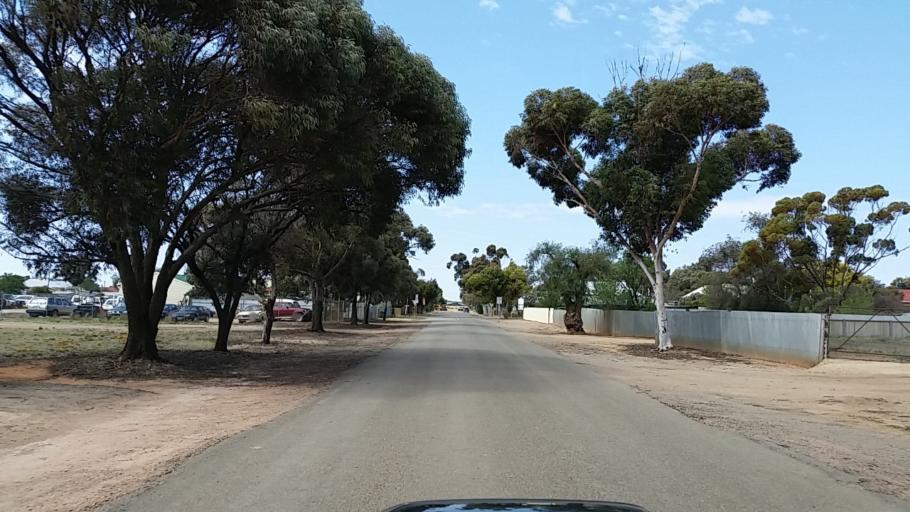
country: AU
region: South Australia
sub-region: Peterborough
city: Peterborough
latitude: -32.9755
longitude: 138.8393
